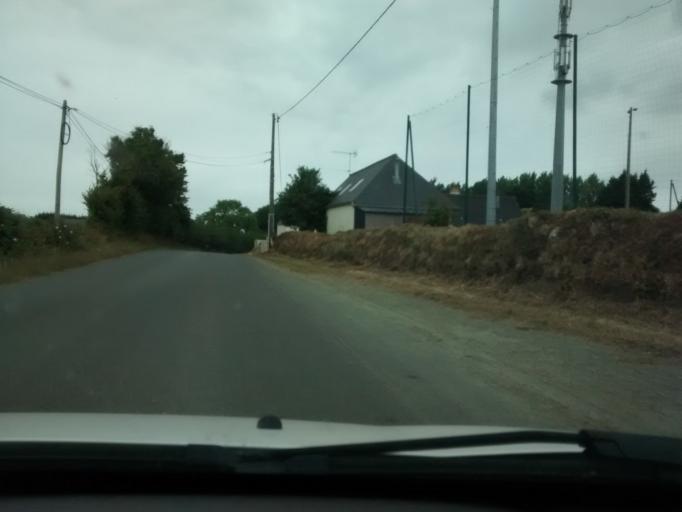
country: FR
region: Brittany
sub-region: Departement des Cotes-d'Armor
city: Trevou-Treguignec
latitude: 48.8095
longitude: -3.3545
